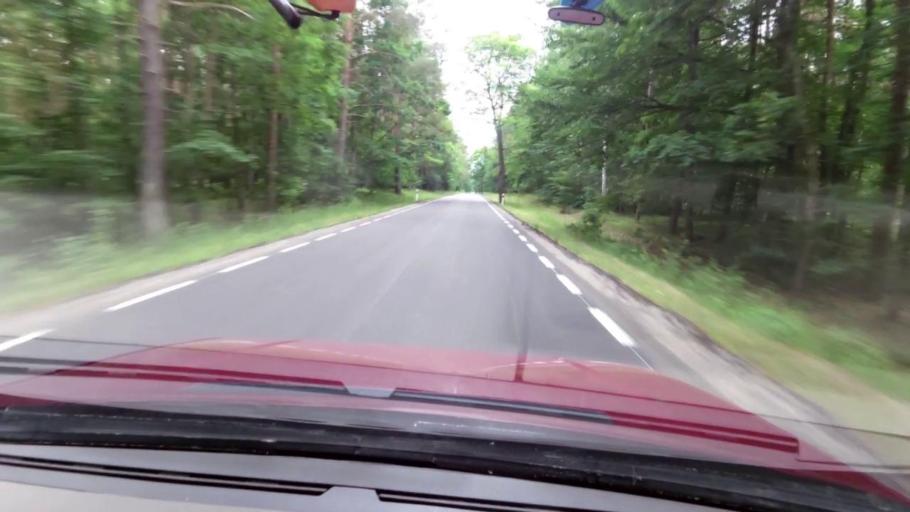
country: PL
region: Pomeranian Voivodeship
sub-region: Powiat slupski
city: Kepice
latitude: 54.2307
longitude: 16.8856
